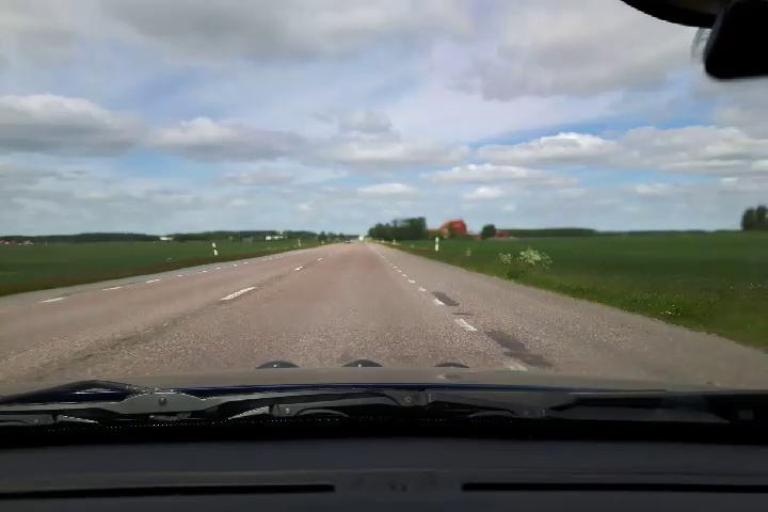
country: SE
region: Uppsala
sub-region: Uppsala Kommun
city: Gamla Uppsala
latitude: 59.9149
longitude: 17.6054
